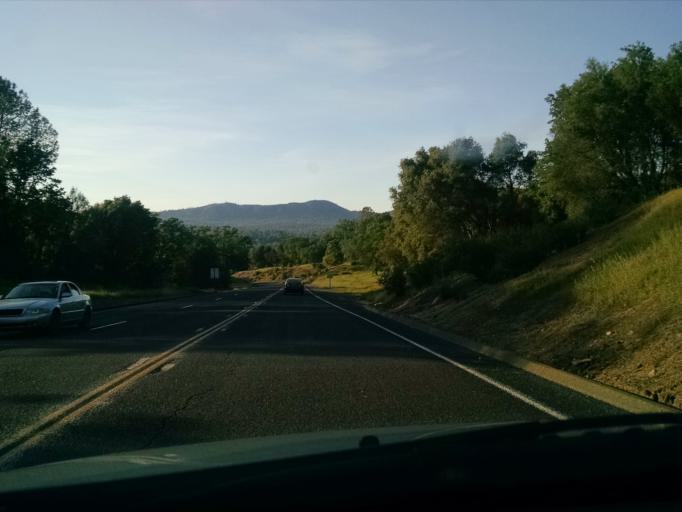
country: US
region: California
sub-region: Mariposa County
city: Mariposa
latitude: 37.4562
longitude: -119.8685
